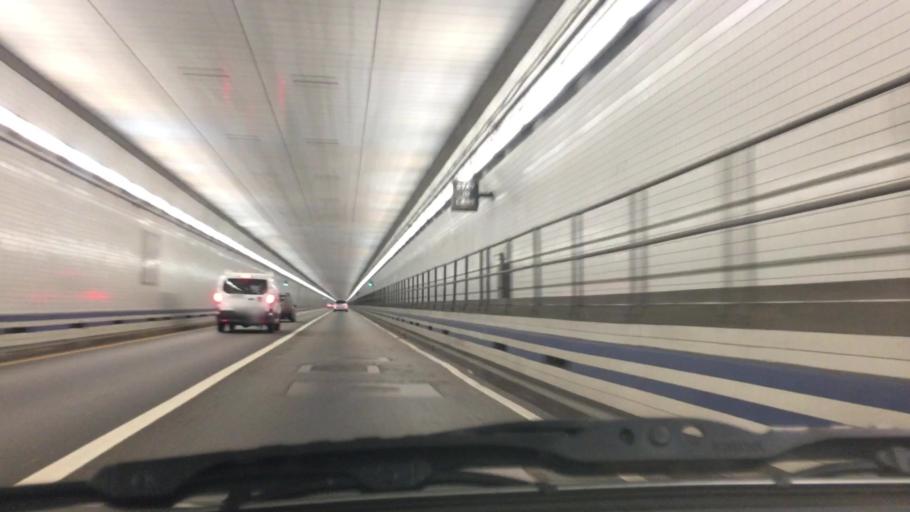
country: US
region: Virginia
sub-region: City of Hampton
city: East Hampton
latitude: 36.9974
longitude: -76.3154
